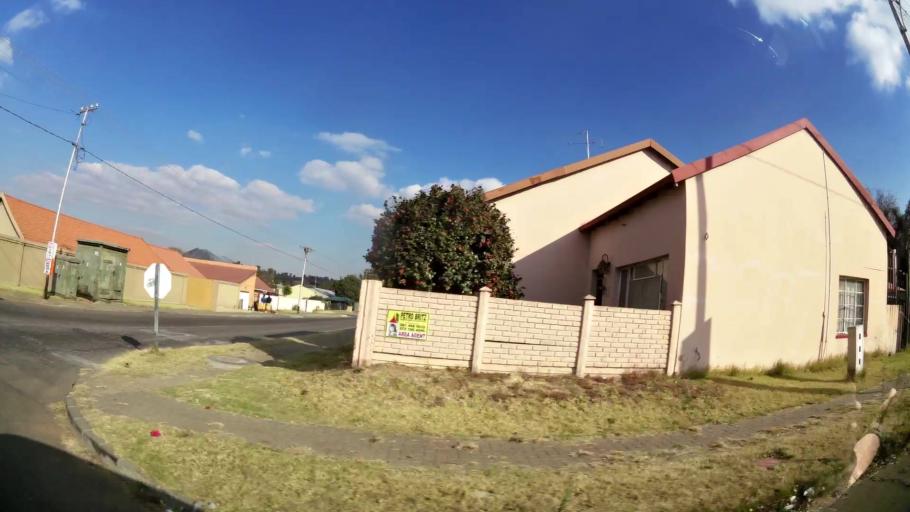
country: ZA
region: Gauteng
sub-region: West Rand District Municipality
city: Krugersdorp
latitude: -26.0931
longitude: 27.7528
